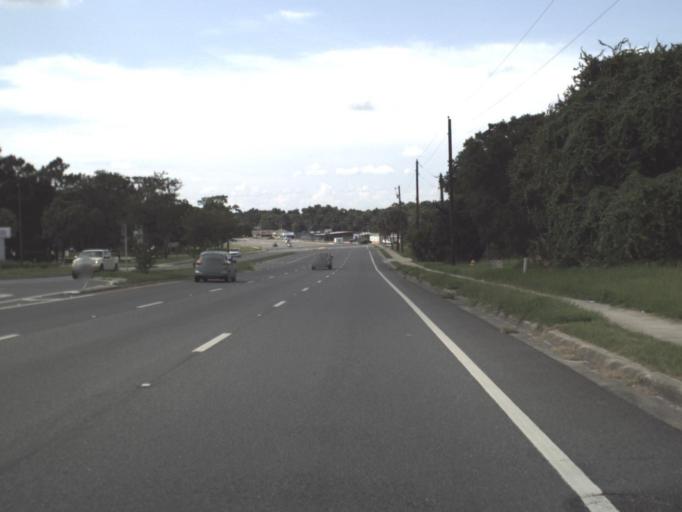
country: US
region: Florida
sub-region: Citrus County
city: Inverness
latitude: 28.8252
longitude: -82.3191
